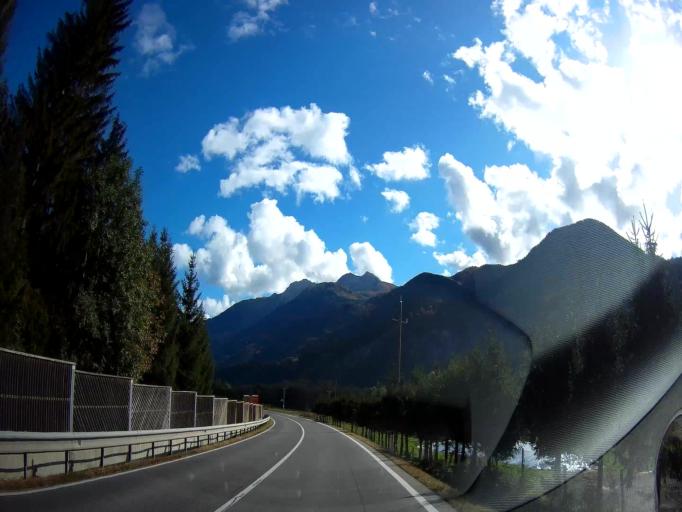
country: AT
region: Carinthia
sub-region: Politischer Bezirk Spittal an der Drau
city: Irschen
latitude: 46.7440
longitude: 12.9998
